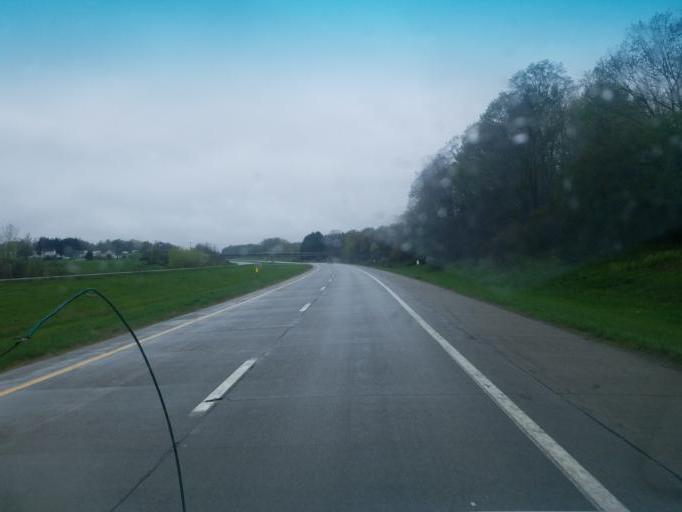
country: US
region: New York
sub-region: Chautauqua County
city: Lakewood
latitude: 42.1531
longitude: -79.4204
